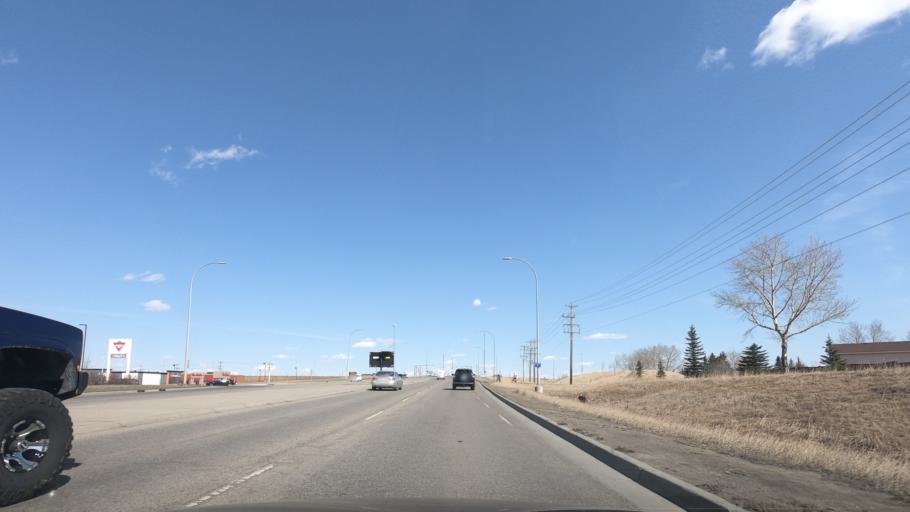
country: CA
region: Alberta
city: Airdrie
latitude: 51.3000
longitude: -114.0084
